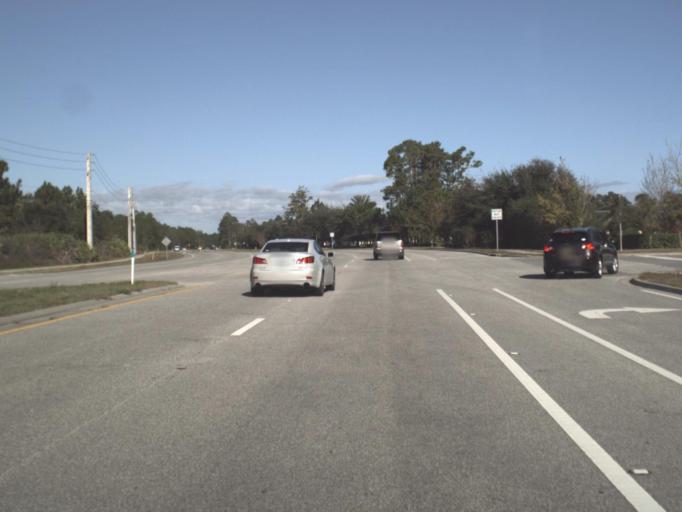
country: US
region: Florida
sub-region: Volusia County
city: Holly Hill
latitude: 29.2286
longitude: -81.0869
